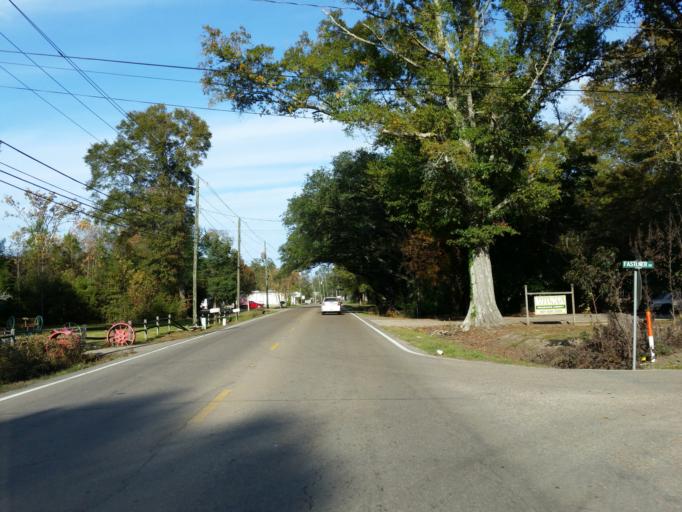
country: US
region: Mississippi
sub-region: Jones County
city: Ellisville
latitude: 31.6511
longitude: -89.1719
